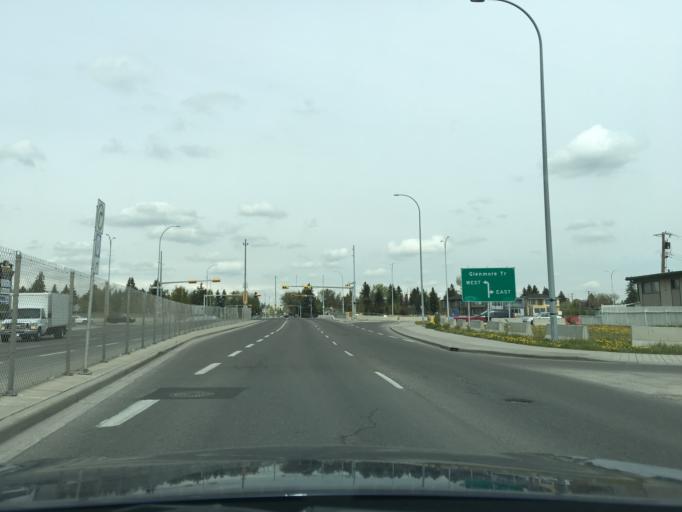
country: CA
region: Alberta
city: Calgary
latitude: 50.9932
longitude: -114.0831
